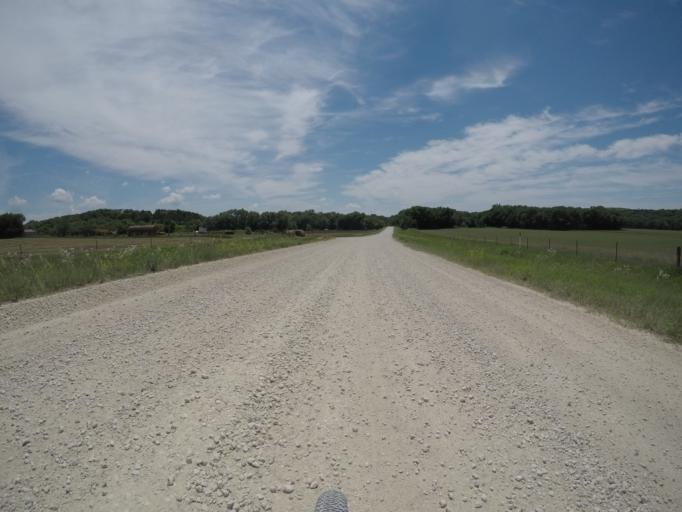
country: US
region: Kansas
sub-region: Wabaunsee County
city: Alma
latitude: 38.9621
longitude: -96.2520
